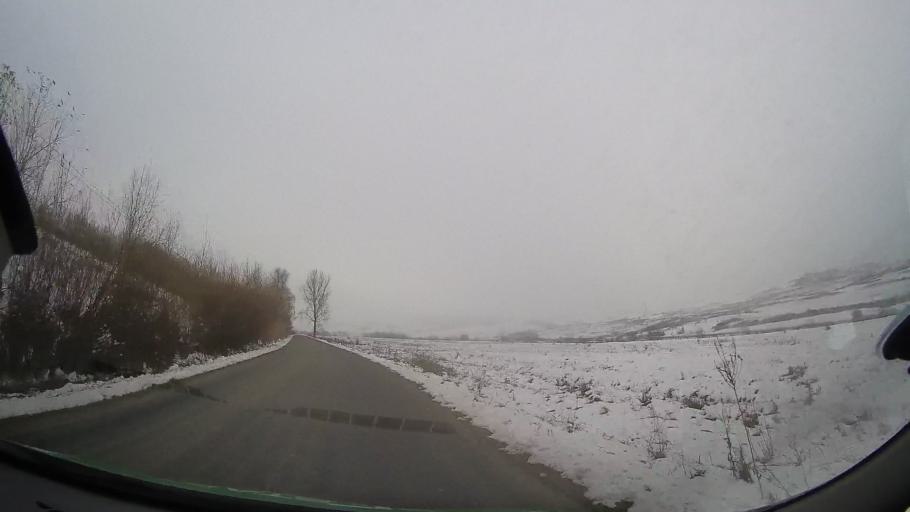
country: RO
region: Bacau
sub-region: Comuna Vultureni
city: Vultureni
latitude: 46.3117
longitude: 27.2926
